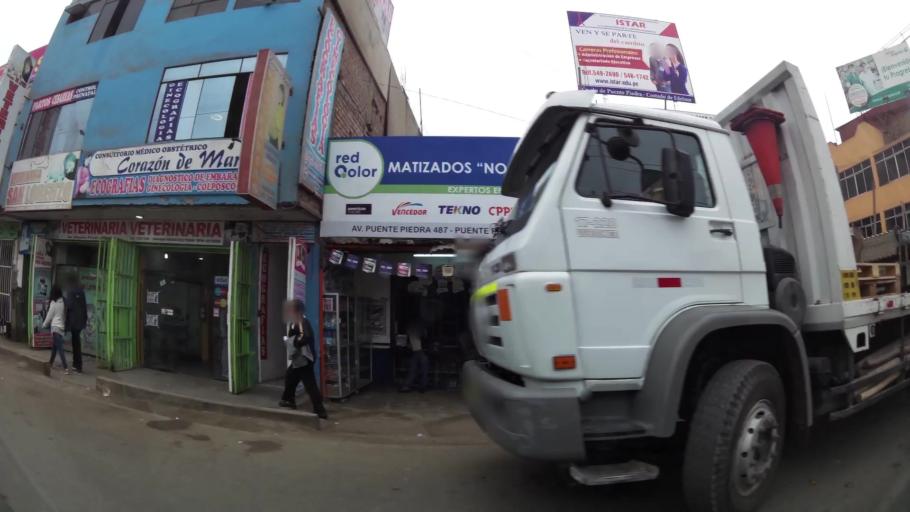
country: PE
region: Lima
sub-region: Lima
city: Carabayllo
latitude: -11.8626
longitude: -77.0770
